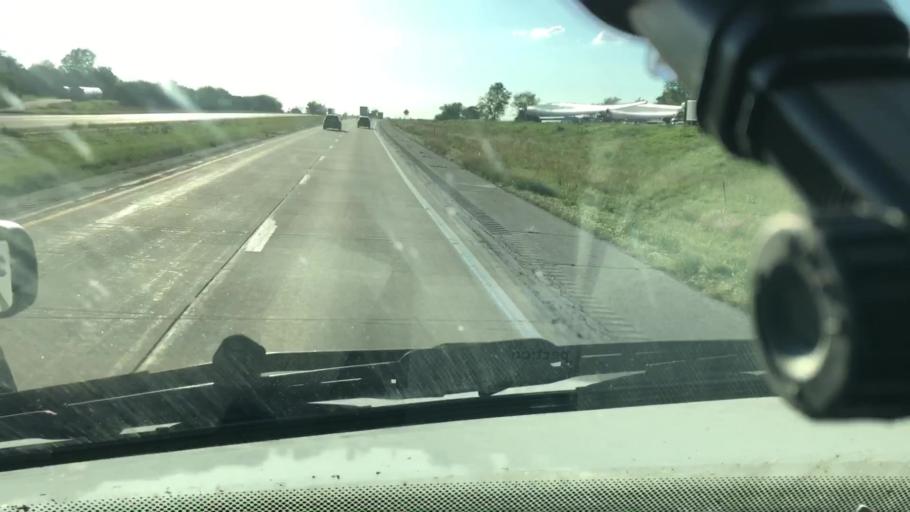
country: US
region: Iowa
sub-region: Pottawattamie County
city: Avoca
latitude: 41.4991
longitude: -95.4910
